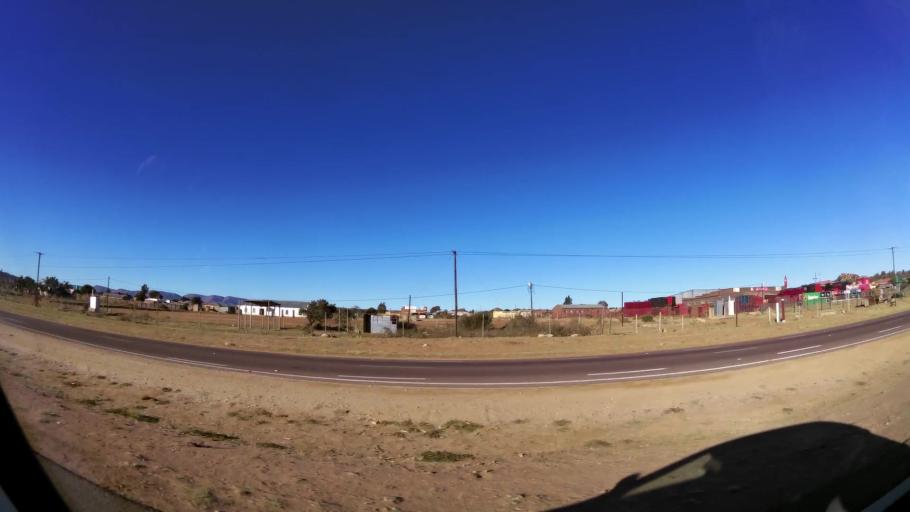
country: ZA
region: Limpopo
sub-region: Capricorn District Municipality
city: Mankoeng
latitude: -23.9112
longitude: 29.7779
